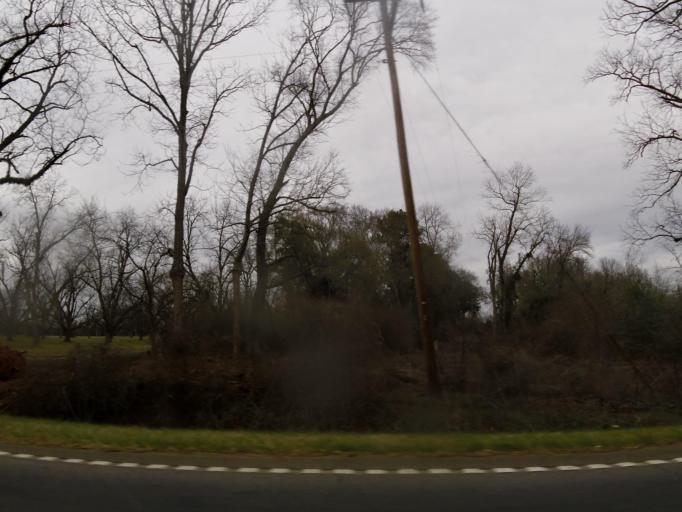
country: US
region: Georgia
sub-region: Terrell County
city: Dawson
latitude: 31.7701
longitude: -84.5125
